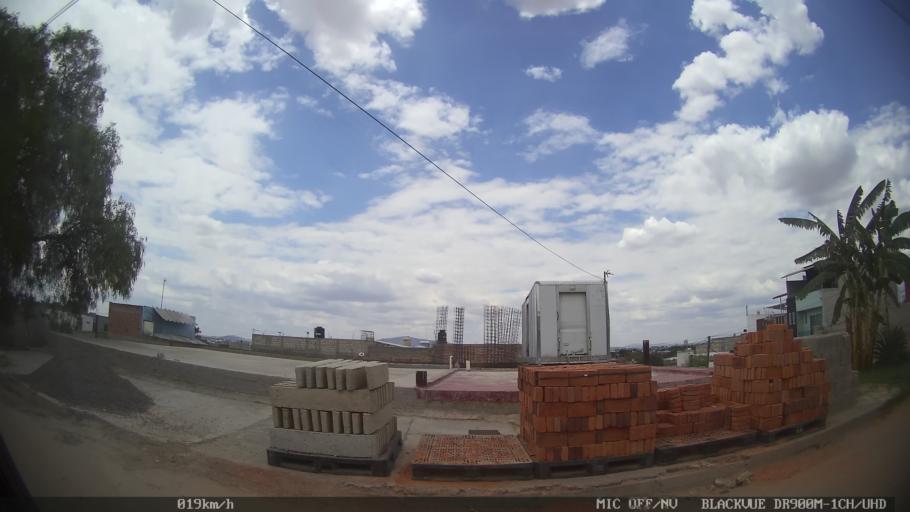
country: MX
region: Jalisco
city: Tlaquepaque
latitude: 20.6368
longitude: -103.2682
